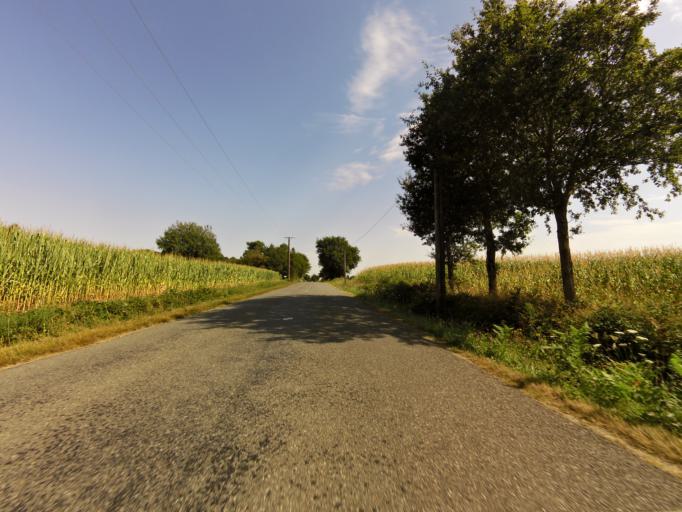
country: FR
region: Brittany
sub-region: Departement du Morbihan
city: Limerzel
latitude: 47.6499
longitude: -2.3831
